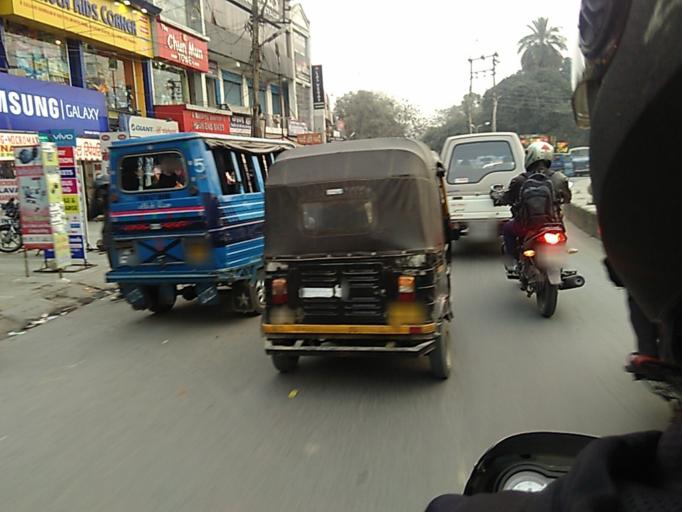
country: IN
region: Uttarakhand
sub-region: Dehradun
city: Dehradun
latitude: 30.3224
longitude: 78.0423
